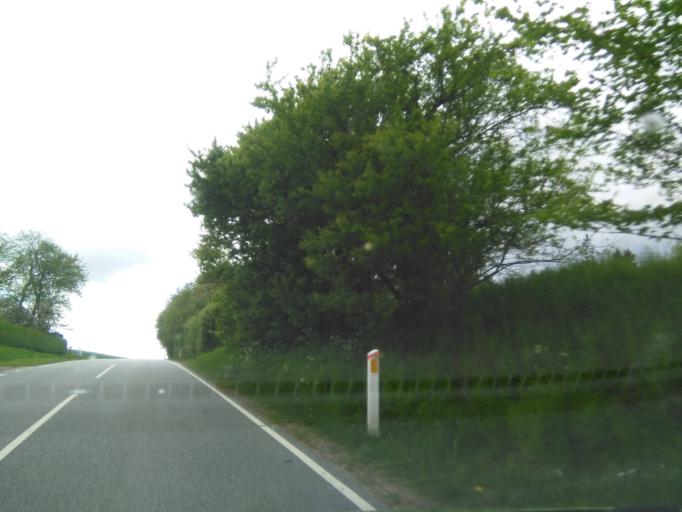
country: DK
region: Central Jutland
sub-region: Horsens Kommune
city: Braedstrup
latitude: 56.0172
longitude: 9.6578
